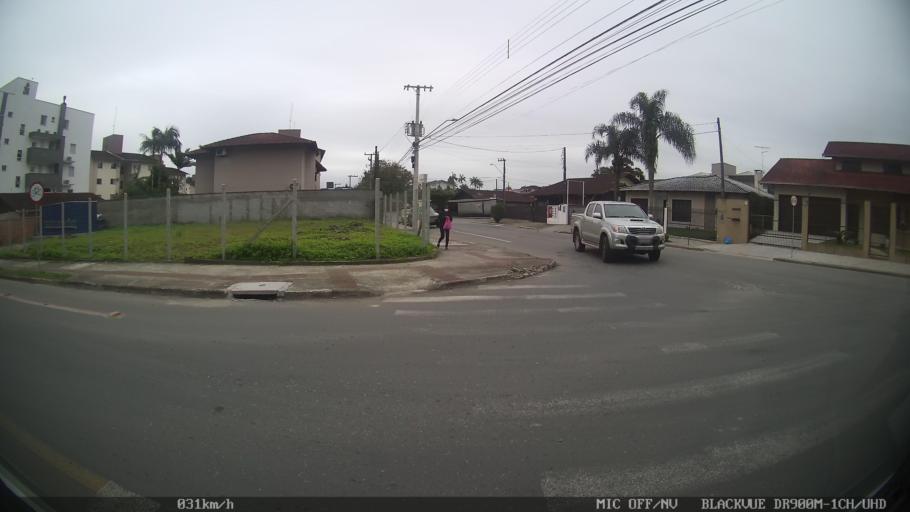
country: BR
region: Santa Catarina
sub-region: Joinville
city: Joinville
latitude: -26.2741
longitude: -48.8399
